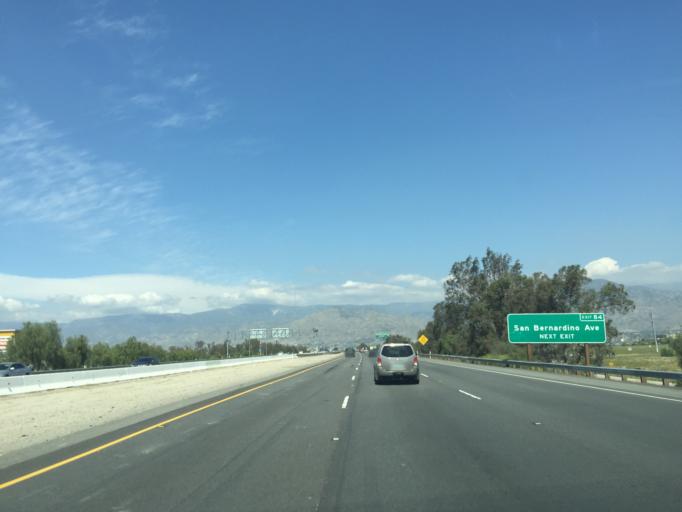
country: US
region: California
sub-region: San Bernardino County
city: Redlands
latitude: 34.0742
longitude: -117.2006
